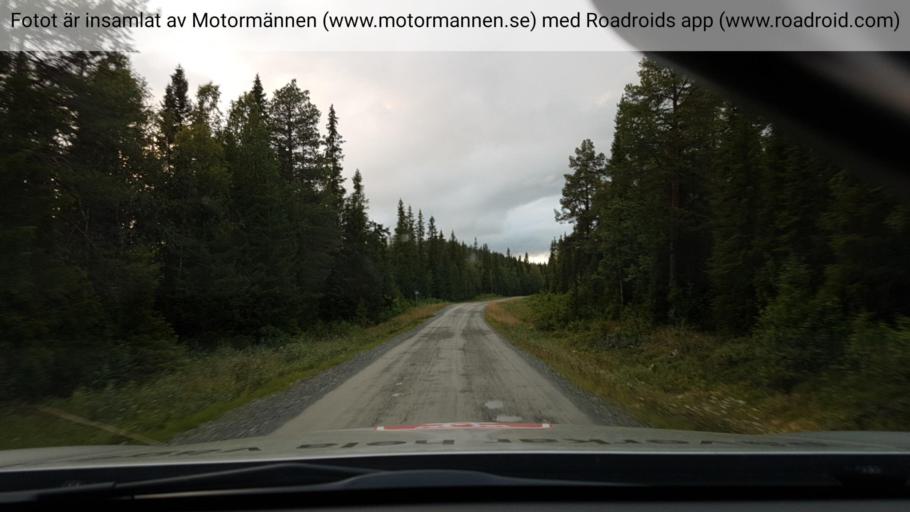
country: SE
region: Vaesterbotten
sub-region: Vilhelmina Kommun
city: Sjoberg
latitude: 65.5267
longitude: 15.4394
